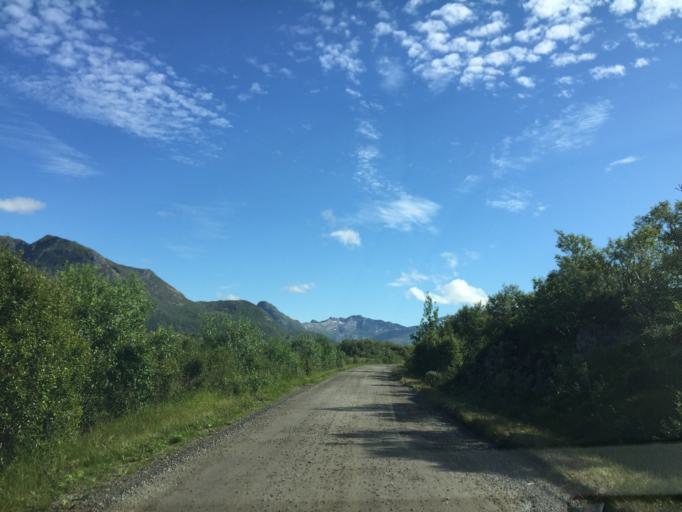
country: NO
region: Nordland
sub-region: Vagan
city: Kabelvag
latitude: 68.3585
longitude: 14.4479
